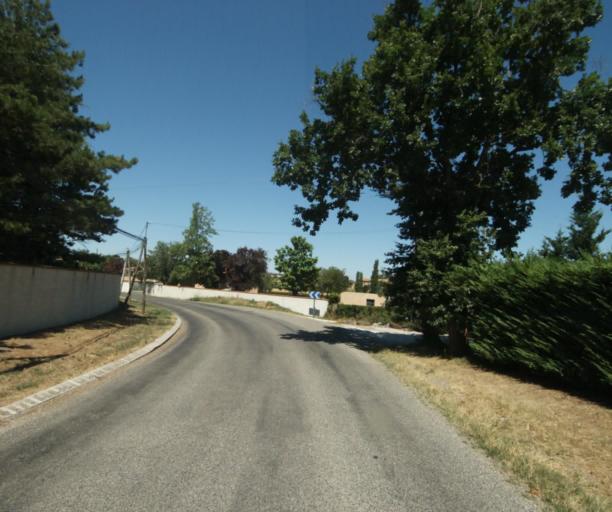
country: FR
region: Midi-Pyrenees
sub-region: Departement de la Haute-Garonne
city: Saint-Felix-Lauragais
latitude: 43.4727
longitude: 1.9305
